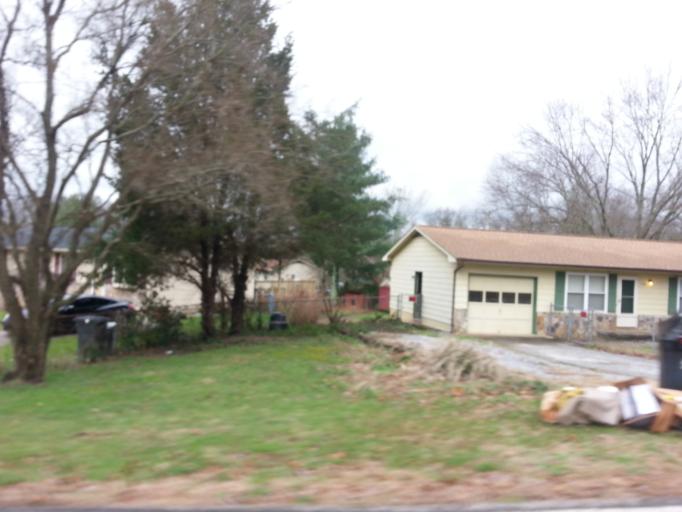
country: US
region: Tennessee
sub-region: Knox County
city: Knoxville
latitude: 35.9943
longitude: -84.0156
